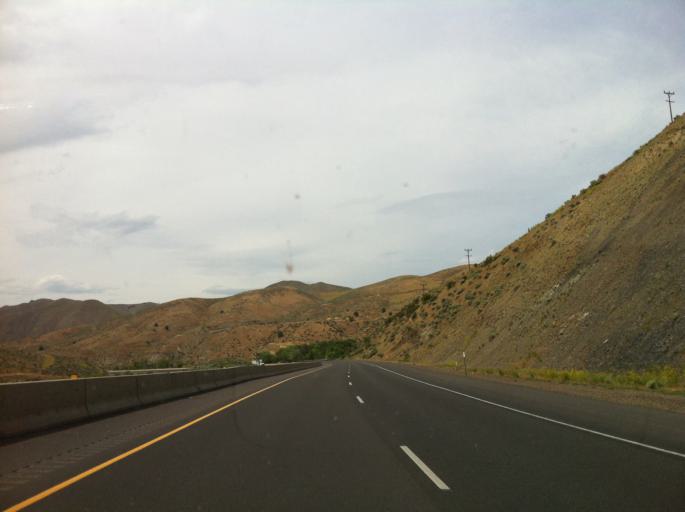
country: US
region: Idaho
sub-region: Washington County
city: Weiser
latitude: 44.4184
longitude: -117.3100
